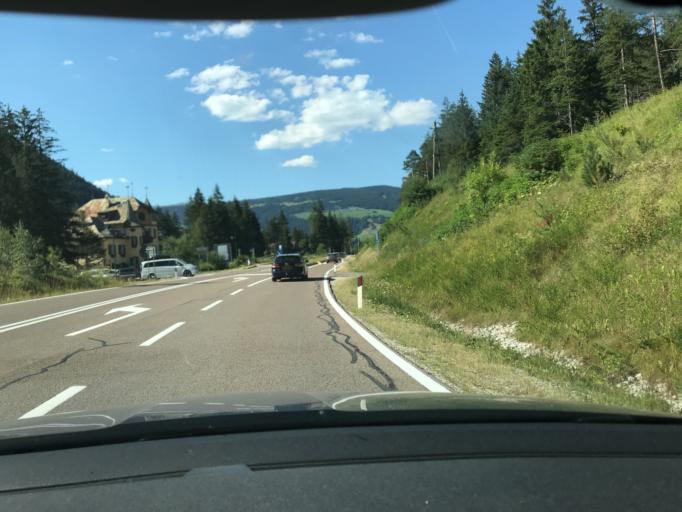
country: IT
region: Trentino-Alto Adige
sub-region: Bolzano
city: Dobbiaco
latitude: 46.7048
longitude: 12.2208
